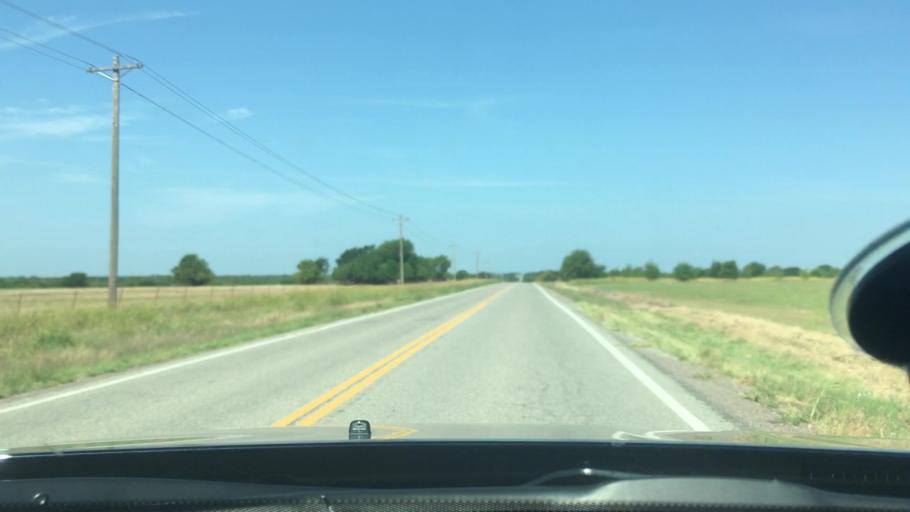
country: US
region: Oklahoma
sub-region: Marshall County
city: Kingston
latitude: 33.9984
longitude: -96.8061
